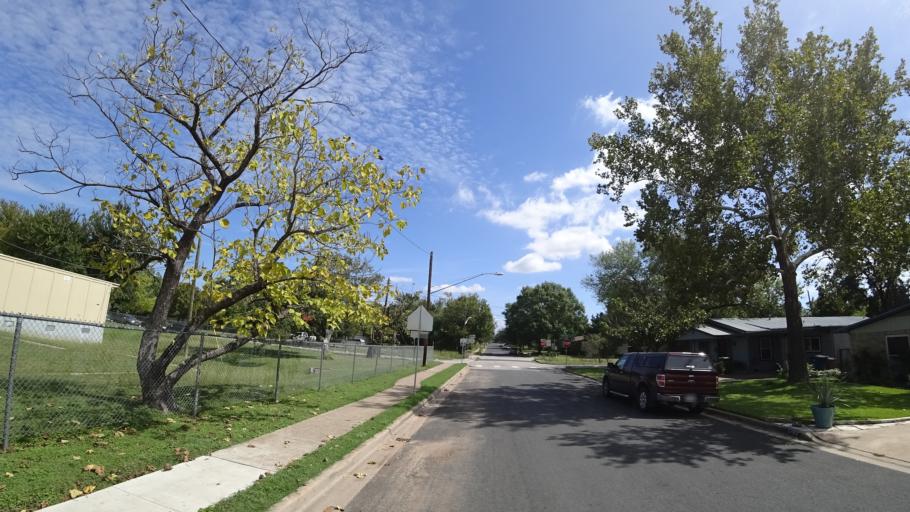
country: US
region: Texas
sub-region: Travis County
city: Austin
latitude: 30.3390
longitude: -97.7318
